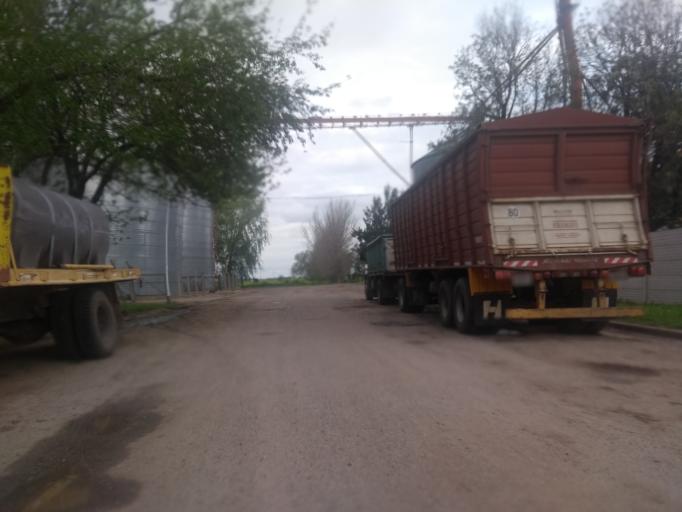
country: AR
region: Santa Fe
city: Galvez
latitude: -31.9070
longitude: -61.2785
